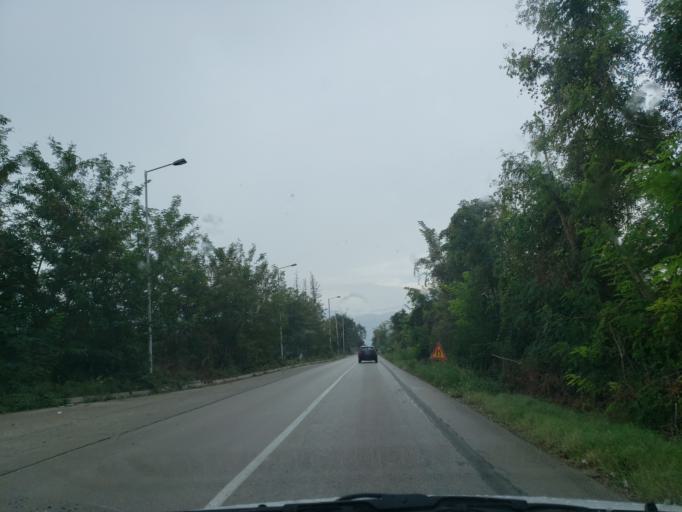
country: GR
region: Central Greece
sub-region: Nomos Fthiotidos
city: Anthili
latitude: 38.8516
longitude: 22.4405
